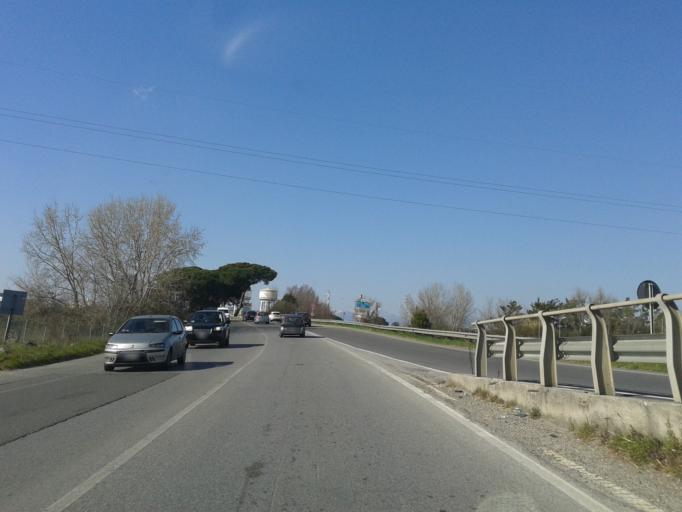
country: IT
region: Tuscany
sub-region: Province of Pisa
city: Pisa
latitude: 43.7008
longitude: 10.3888
